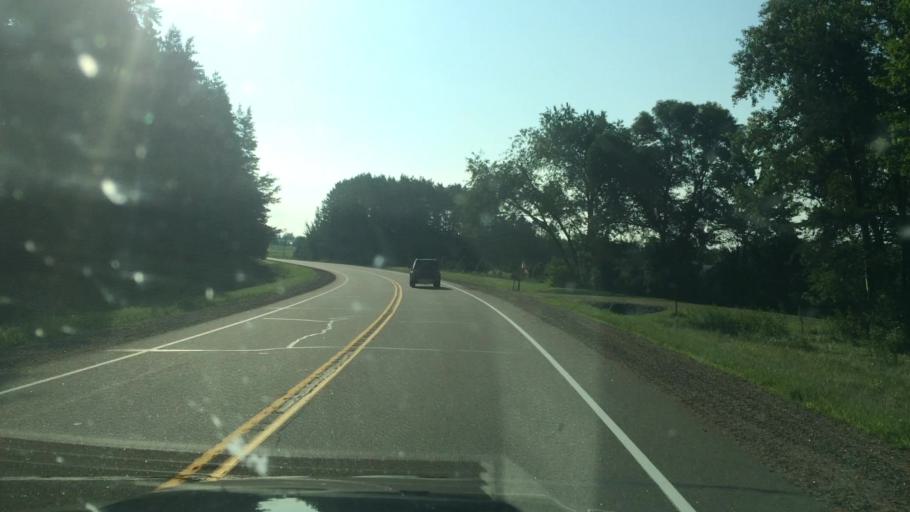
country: US
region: Wisconsin
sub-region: Langlade County
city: Antigo
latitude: 45.1404
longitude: -89.2349
